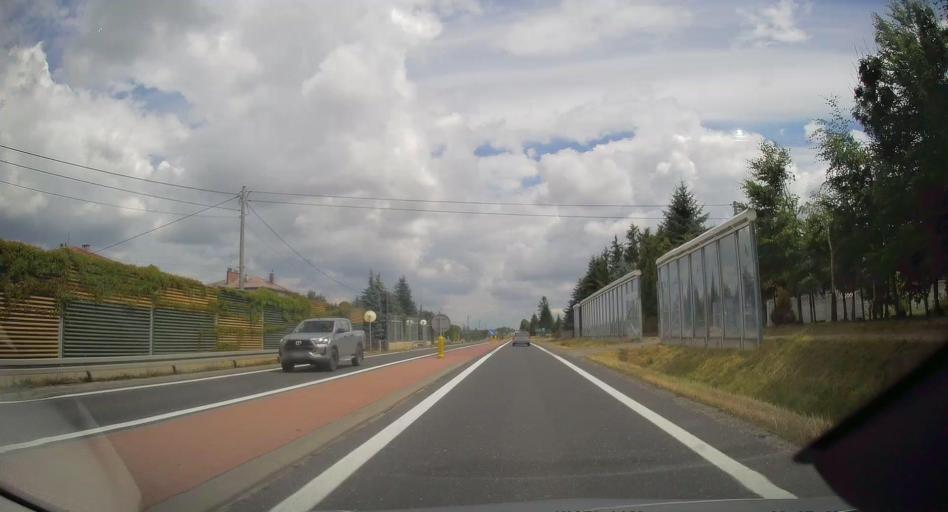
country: PL
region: Subcarpathian Voivodeship
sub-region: Powiat ropczycko-sedziszowski
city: Ostrow
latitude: 50.0621
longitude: 21.5405
